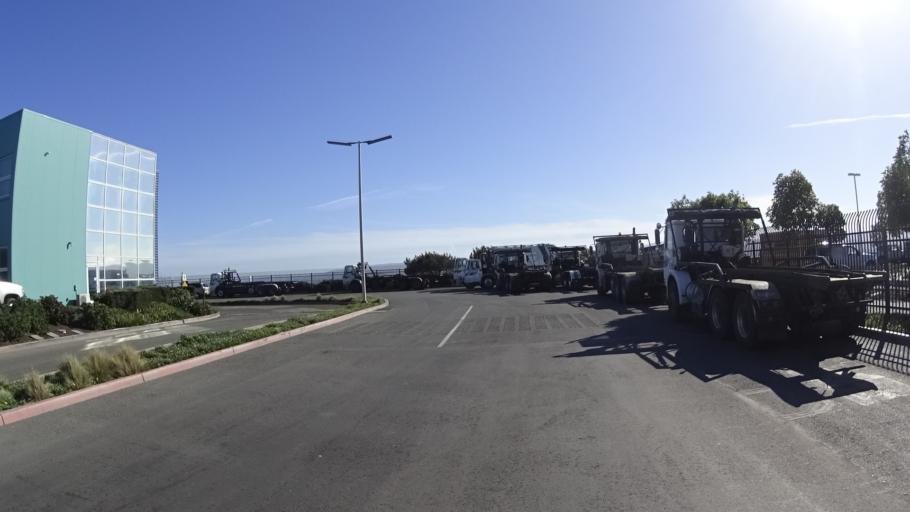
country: US
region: California
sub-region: San Mateo County
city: South San Francisco
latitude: 37.6488
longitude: -122.3839
